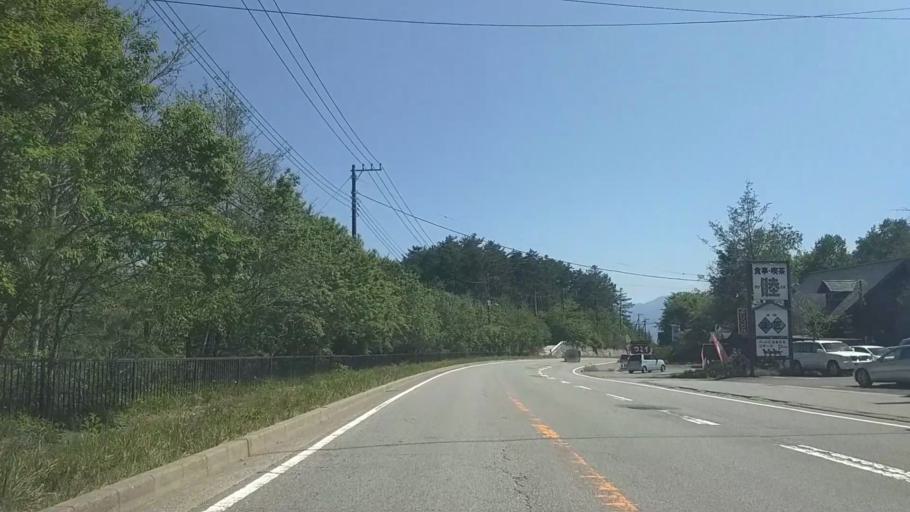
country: JP
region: Yamanashi
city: Nirasaki
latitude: 35.8920
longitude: 138.4403
